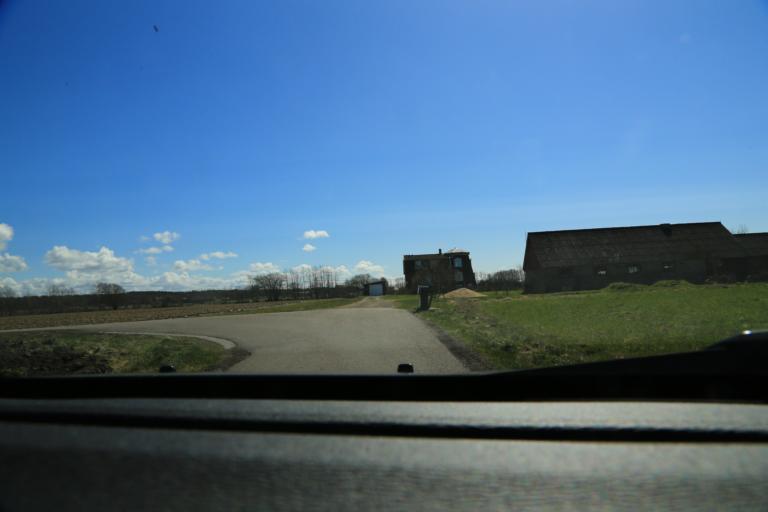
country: SE
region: Halland
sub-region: Varbergs Kommun
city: Traslovslage
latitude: 57.0895
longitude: 12.2976
